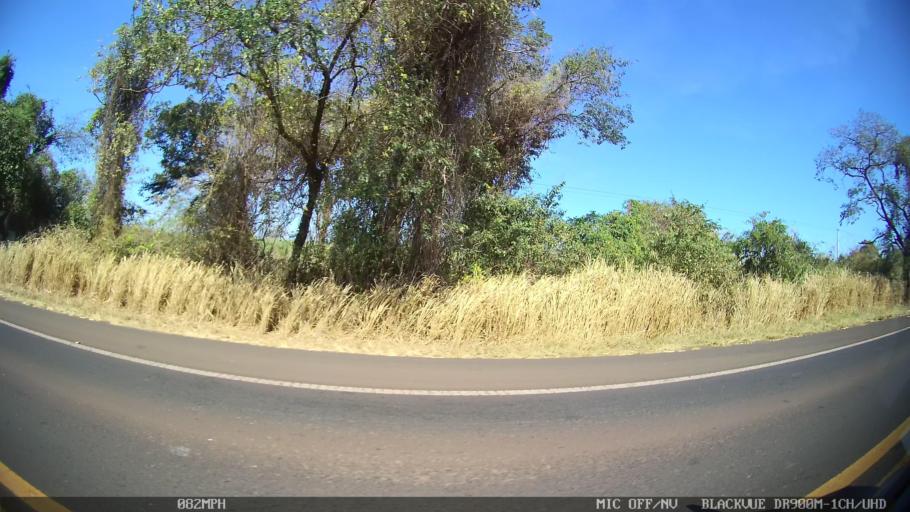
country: BR
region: Sao Paulo
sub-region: Barretos
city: Barretos
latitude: -20.5512
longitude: -48.6345
